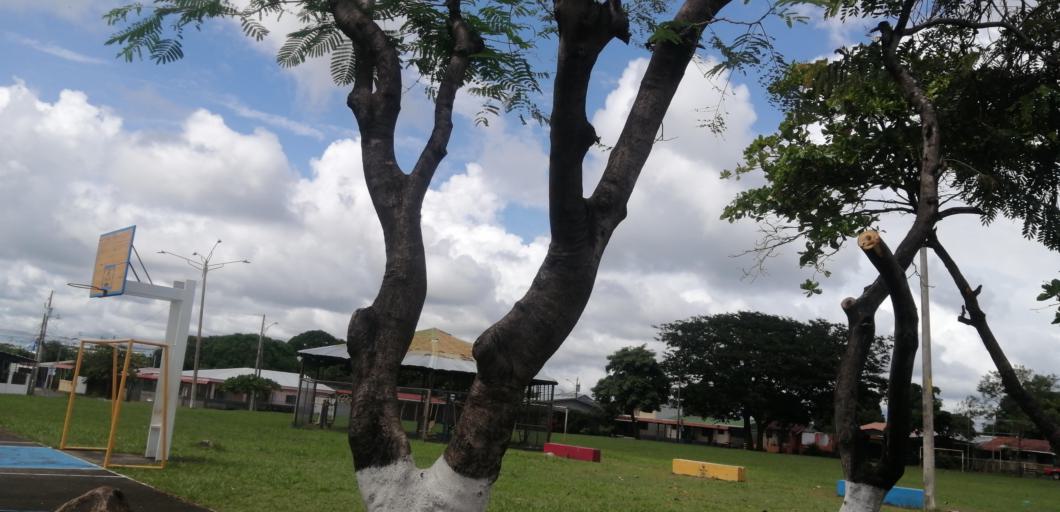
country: CR
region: Guanacaste
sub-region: Canton de Canas
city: Canas
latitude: 10.4316
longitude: -85.0910
